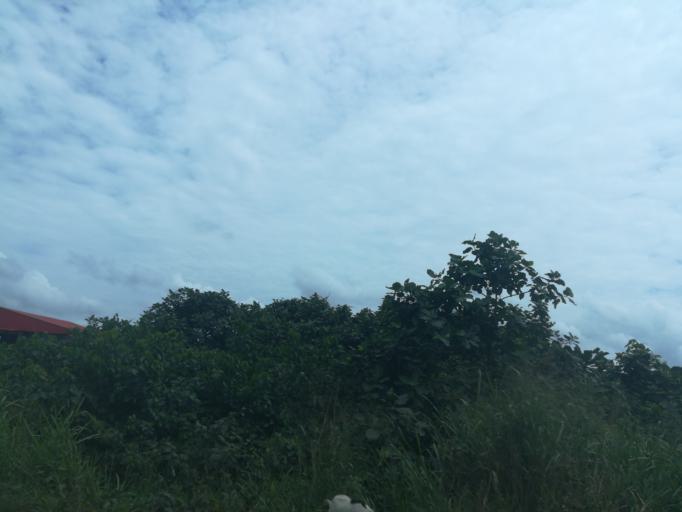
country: NG
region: Lagos
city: Ikotun
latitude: 6.4947
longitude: 3.1312
